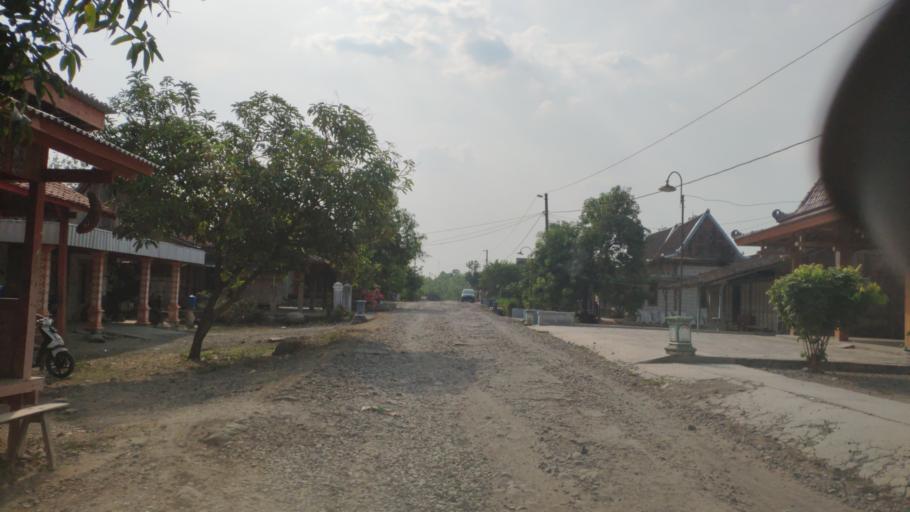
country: ID
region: Central Java
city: Randublatung
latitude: -7.2827
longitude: 111.2534
